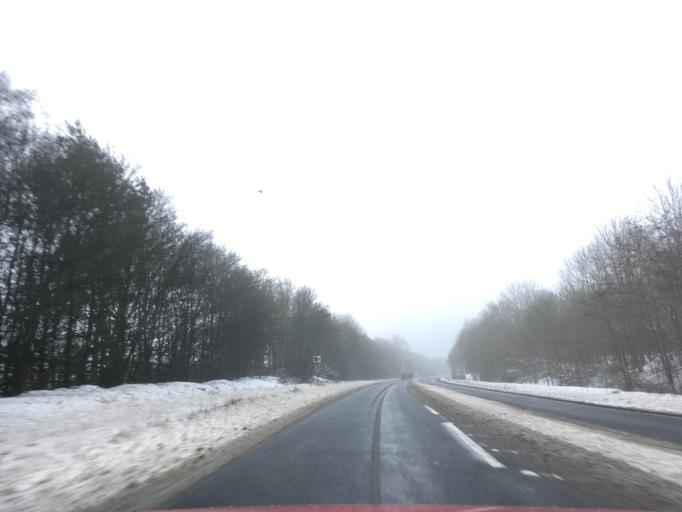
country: GB
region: England
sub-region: Warwickshire
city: Stratford-upon-Avon
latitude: 52.2290
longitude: -1.6971
